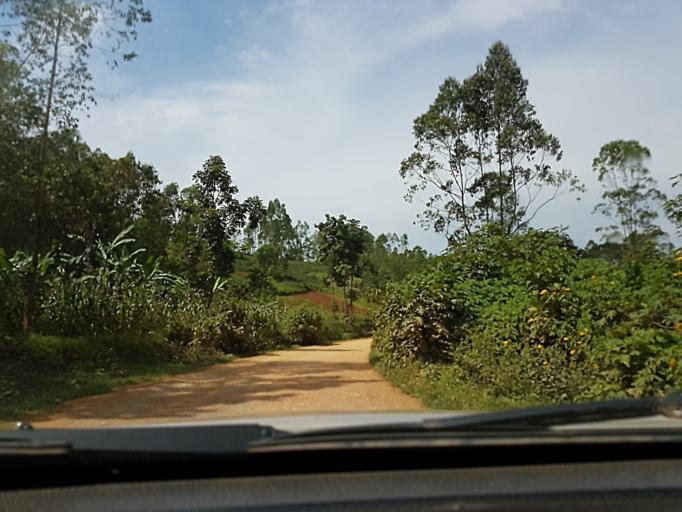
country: CD
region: South Kivu
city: Bukavu
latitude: -2.6445
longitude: 28.8772
